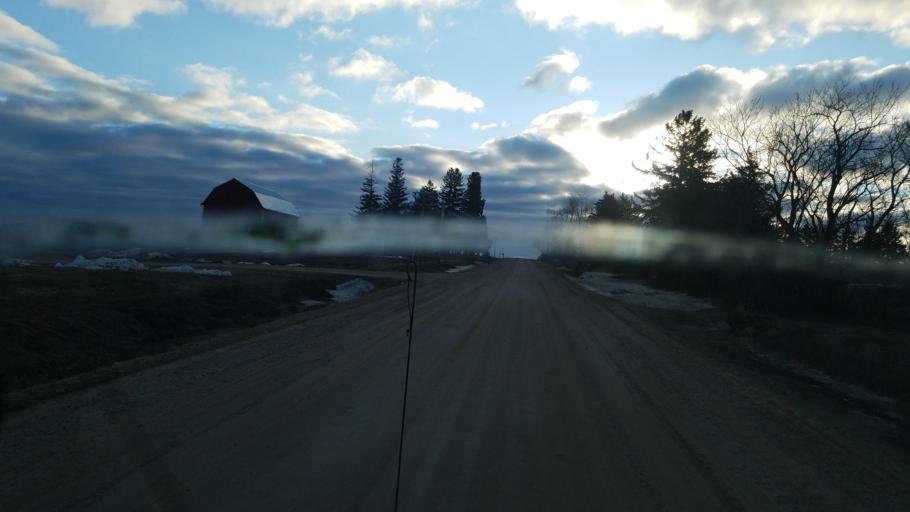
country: US
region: Wisconsin
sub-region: Clark County
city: Loyal
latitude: 44.6110
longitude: -90.4446
